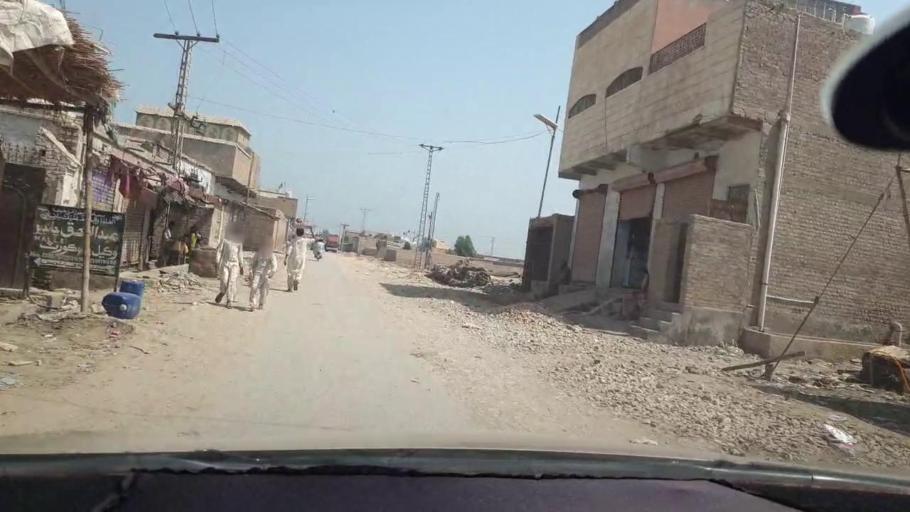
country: PK
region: Sindh
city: Kambar
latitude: 27.5961
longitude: 67.9970
